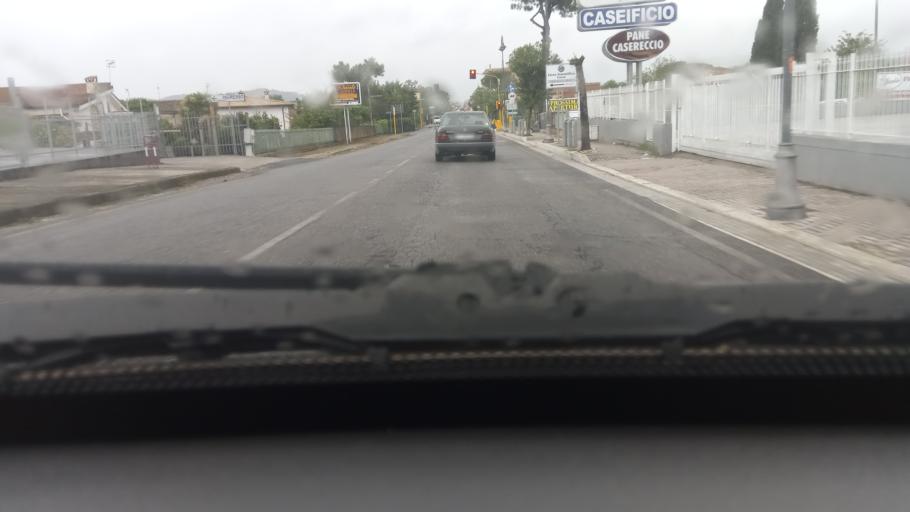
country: IT
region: Latium
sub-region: Provincia di Latina
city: Minturno
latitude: 41.2510
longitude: 13.7315
